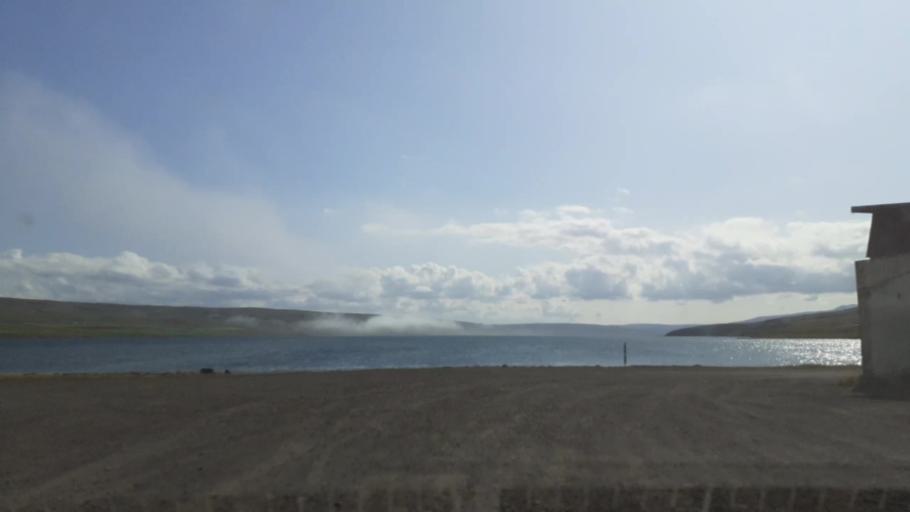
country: IS
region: West
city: Borgarnes
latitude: 65.2094
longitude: -21.0944
